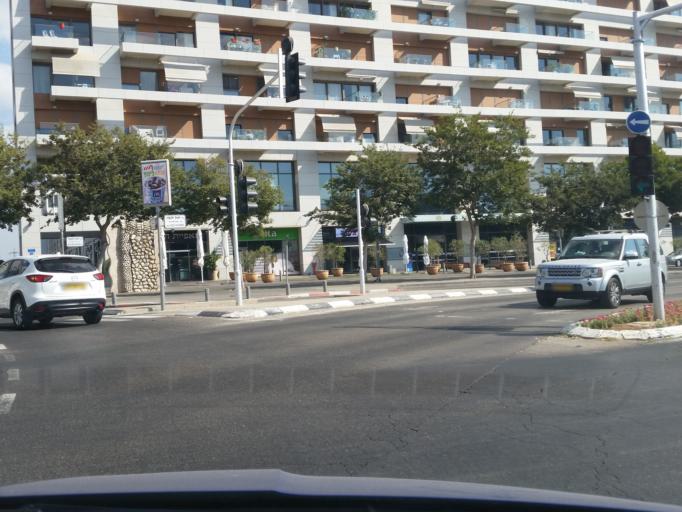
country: IL
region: Tel Aviv
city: Ramat HaSharon
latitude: 32.1145
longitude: 34.8405
